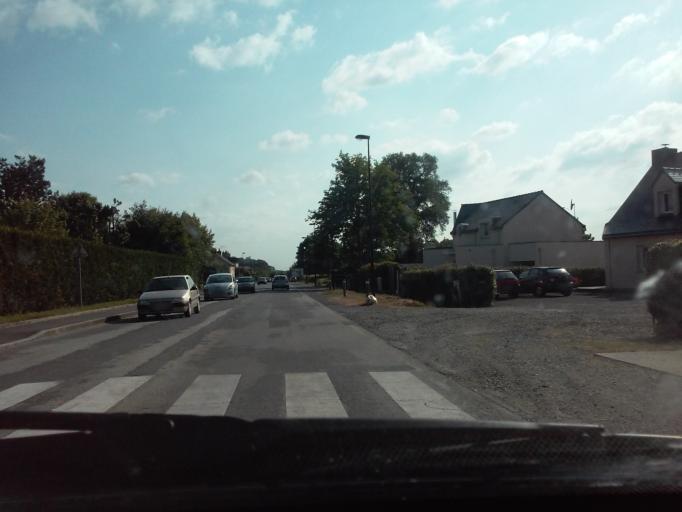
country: FR
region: Brittany
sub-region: Departement d'Ille-et-Vilaine
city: Liffre
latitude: 48.2057
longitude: -1.5216
